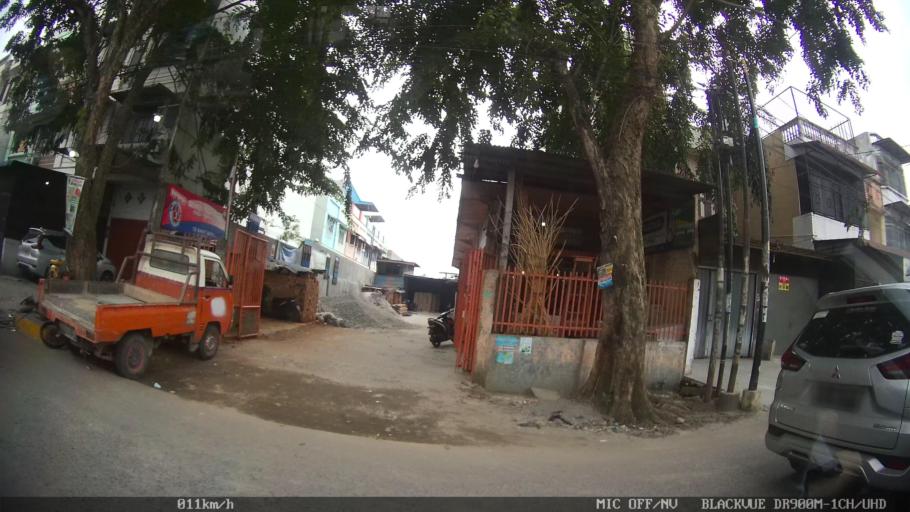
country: ID
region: North Sumatra
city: Medan
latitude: 3.5819
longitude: 98.7067
